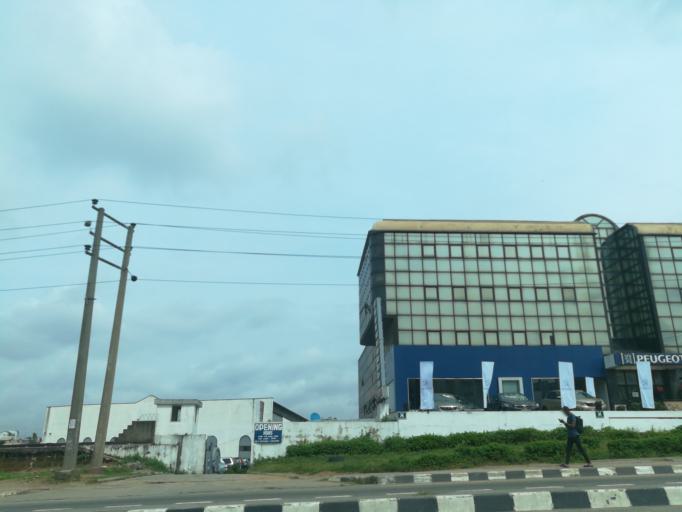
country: NG
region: Lagos
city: Ikeja
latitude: 6.6131
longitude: 3.3548
